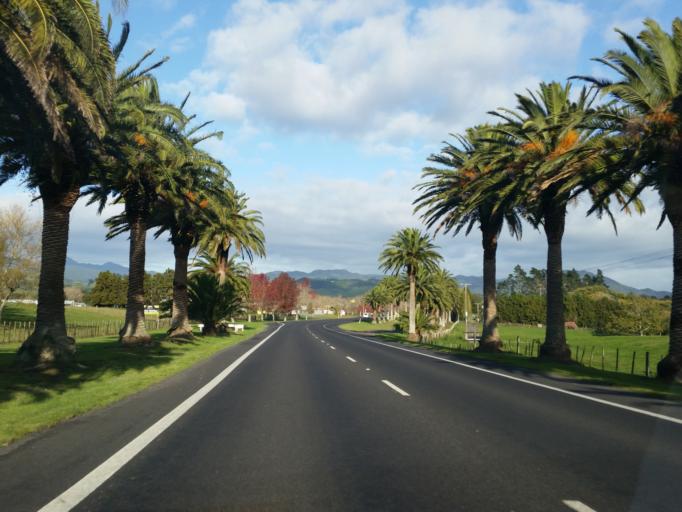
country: NZ
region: Waikato
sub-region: Hauraki District
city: Waihi
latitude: -37.3988
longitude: 175.8257
